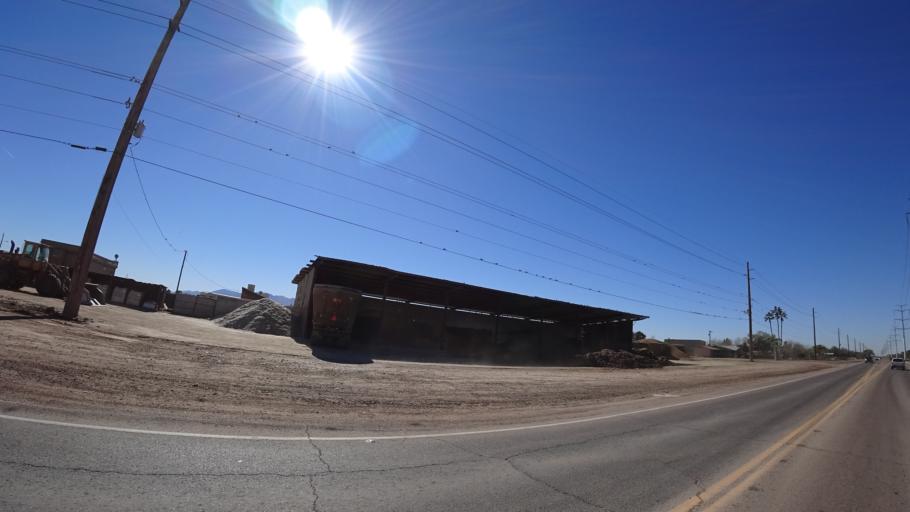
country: US
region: Arizona
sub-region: Maricopa County
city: Laveen
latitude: 33.4085
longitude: -112.2071
